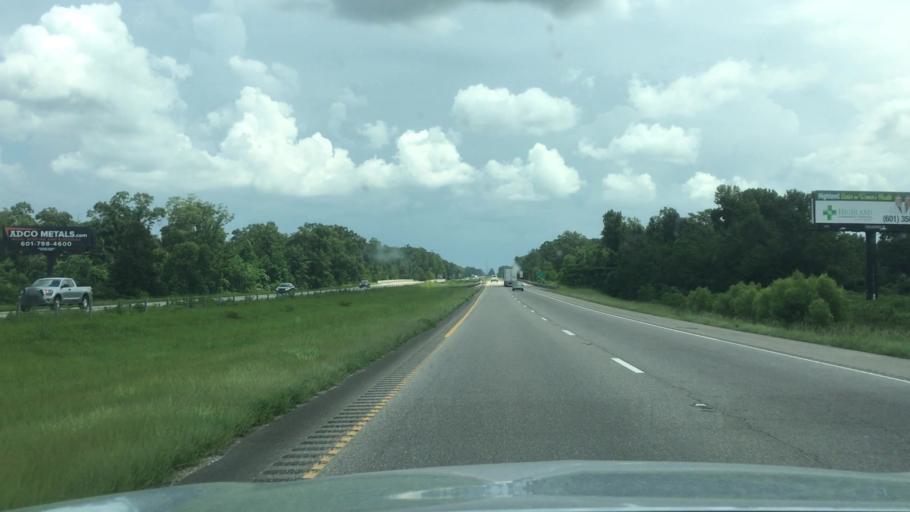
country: US
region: Mississippi
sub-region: Pearl River County
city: Picayune
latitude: 30.5258
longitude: -89.6591
